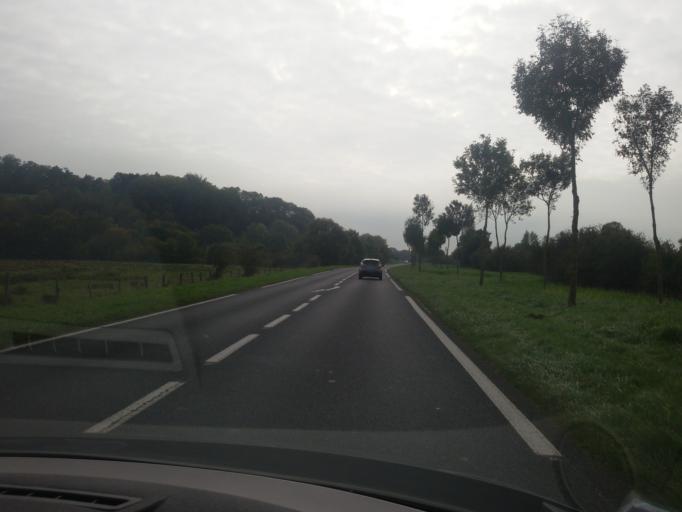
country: FR
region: Lower Normandy
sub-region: Departement du Calvados
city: Dives-sur-Mer
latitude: 49.2522
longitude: -0.1032
